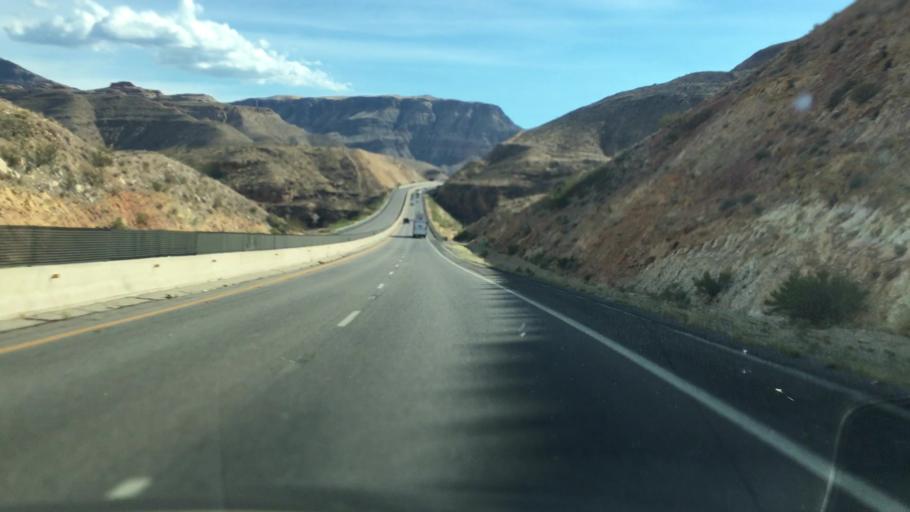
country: US
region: Arizona
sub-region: Mohave County
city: Beaver Dam
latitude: 36.9690
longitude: -113.7550
